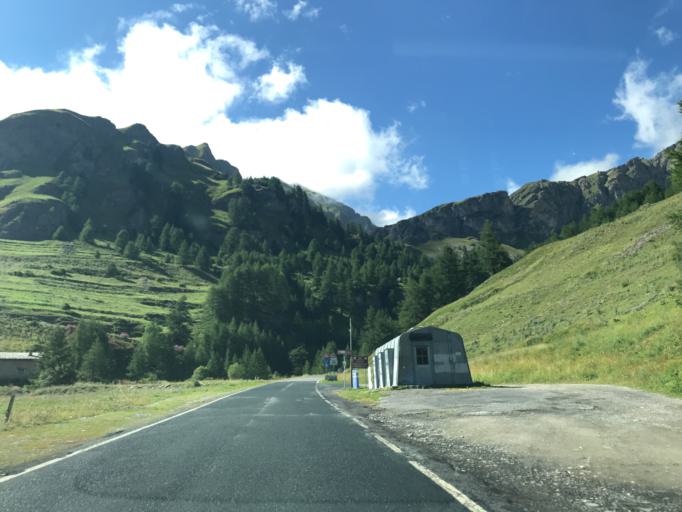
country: IT
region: Piedmont
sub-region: Provincia di Cuneo
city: Pontechianale
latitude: 44.6524
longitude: 6.9927
